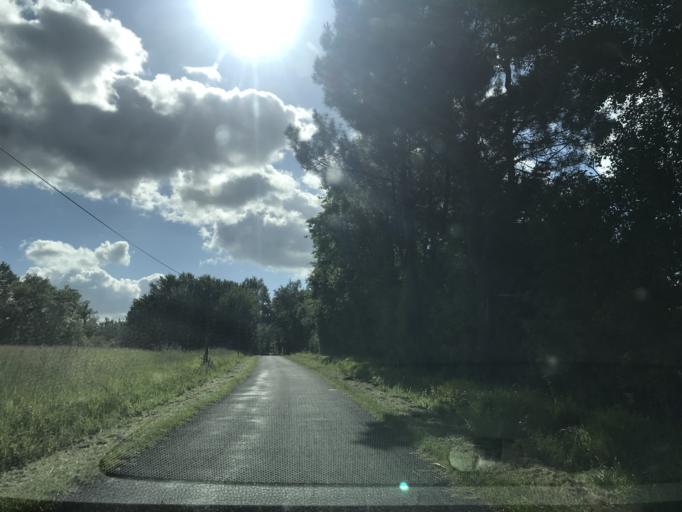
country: FR
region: Poitou-Charentes
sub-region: Departement de la Charente
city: Chalais
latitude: 45.2757
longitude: -0.0306
